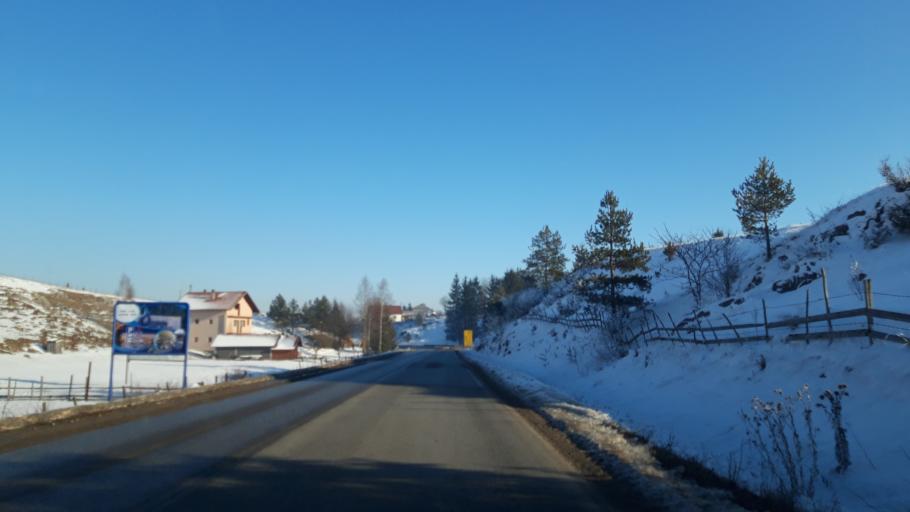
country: BA
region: Republika Srpska
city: Sokolac
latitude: 43.9183
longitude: 18.7632
